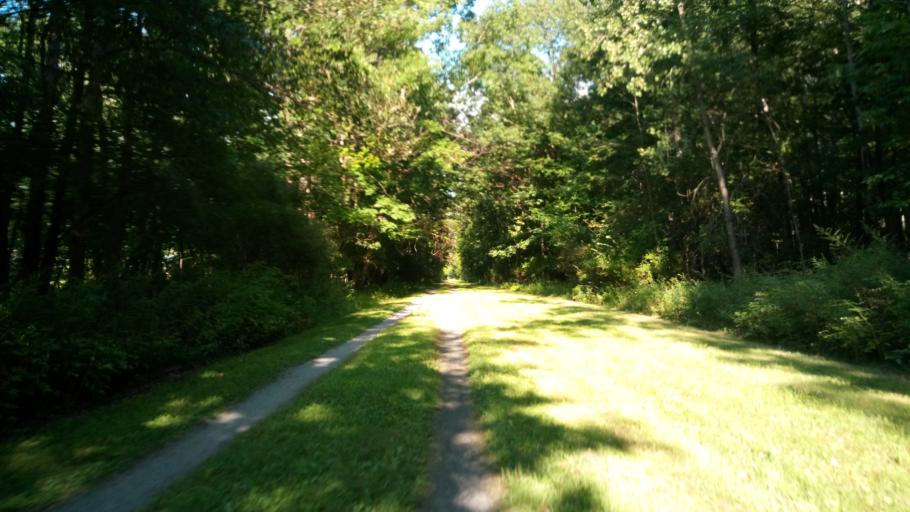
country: US
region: New York
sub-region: Monroe County
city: Honeoye Falls
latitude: 42.9890
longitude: -77.5420
